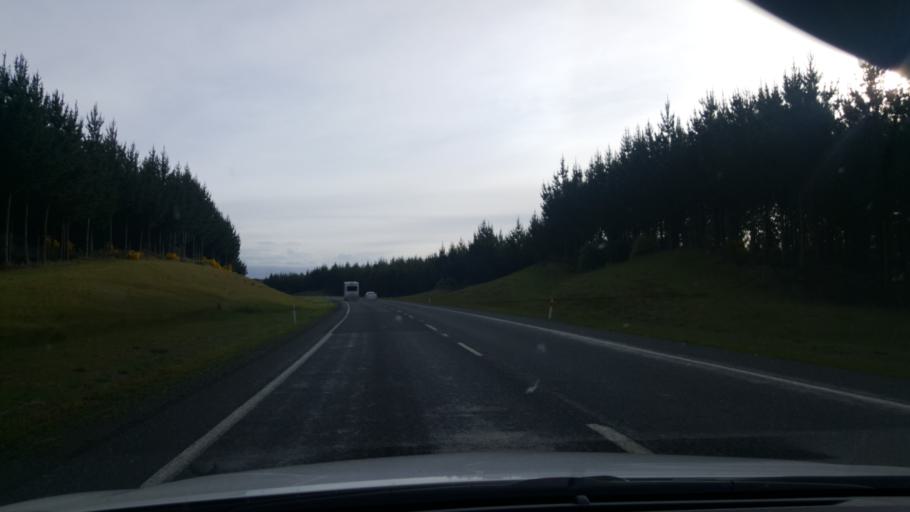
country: NZ
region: Waikato
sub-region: Taupo District
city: Taupo
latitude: -38.8249
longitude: 176.0696
